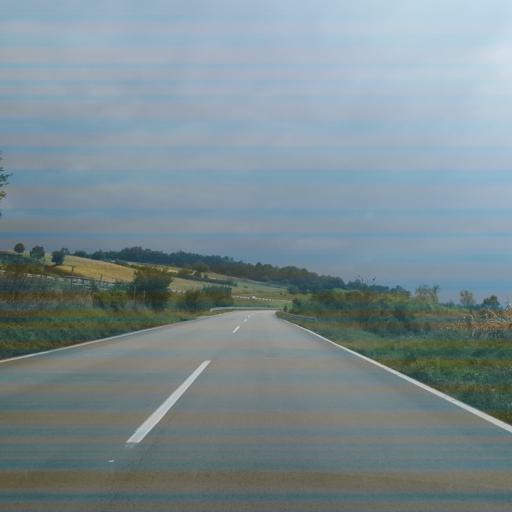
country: RS
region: Central Serbia
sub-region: Nisavski Okrug
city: Razanj
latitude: 43.6542
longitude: 21.5529
